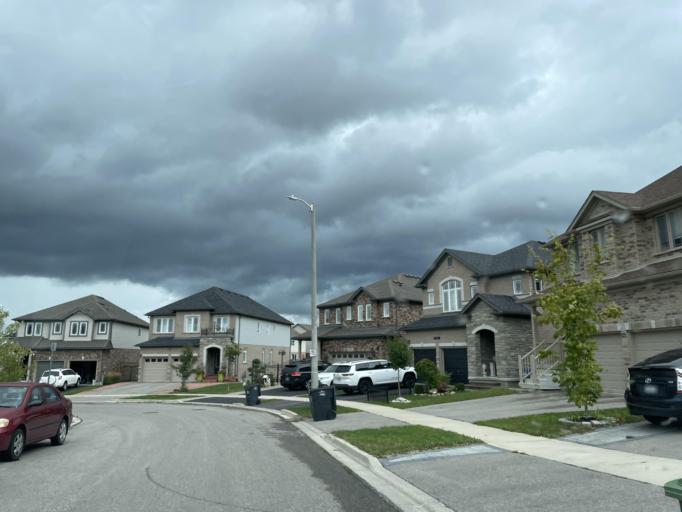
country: CA
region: Ontario
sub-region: Wellington County
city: Guelph
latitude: 43.5207
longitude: -80.3065
